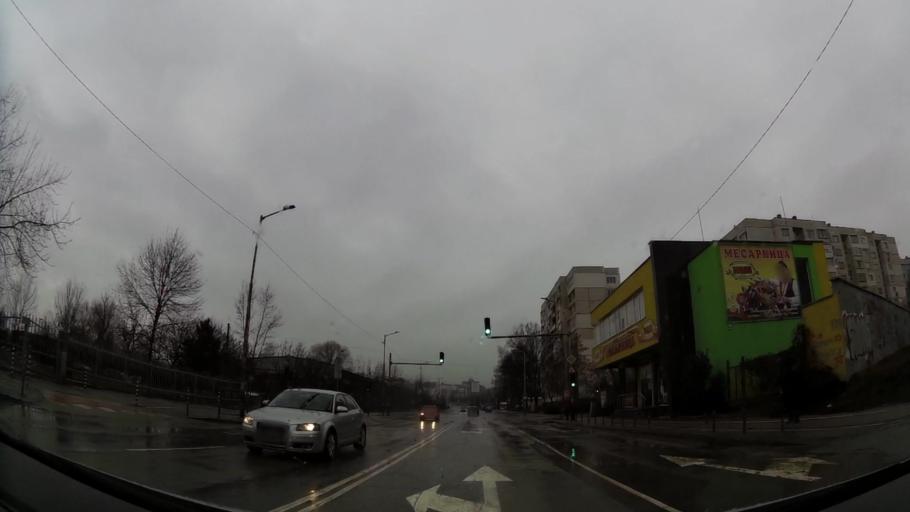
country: BG
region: Sofia-Capital
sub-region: Stolichna Obshtina
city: Sofia
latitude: 42.6336
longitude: 23.3803
